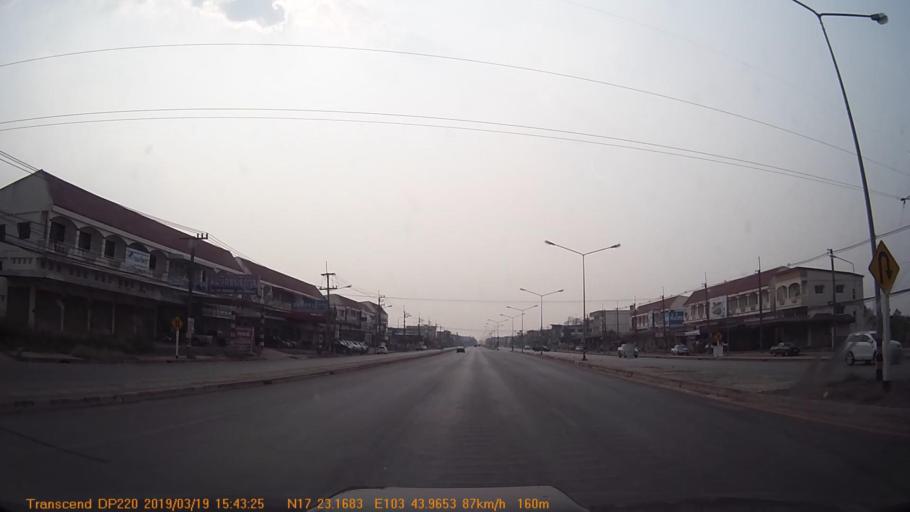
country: TH
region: Sakon Nakhon
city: Phang Khon
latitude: 17.3862
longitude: 103.7325
